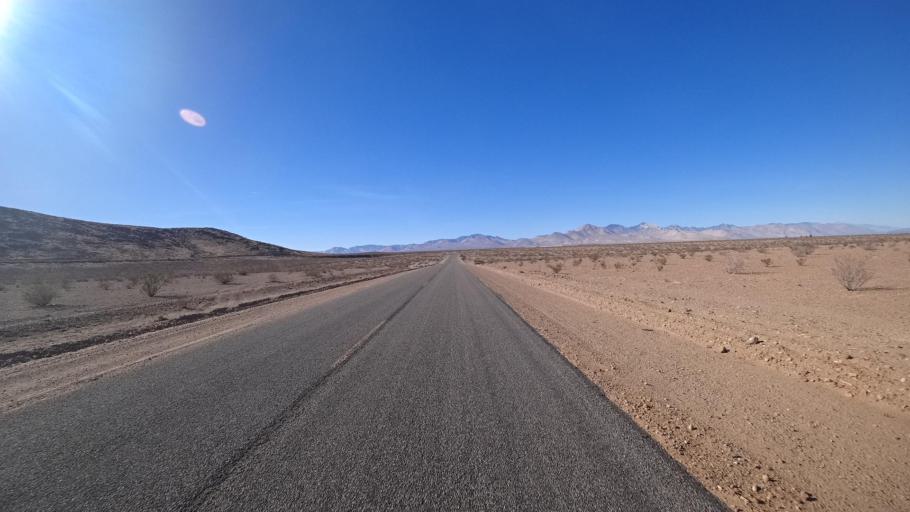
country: US
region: California
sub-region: Kern County
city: China Lake Acres
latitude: 35.5604
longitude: -117.7691
